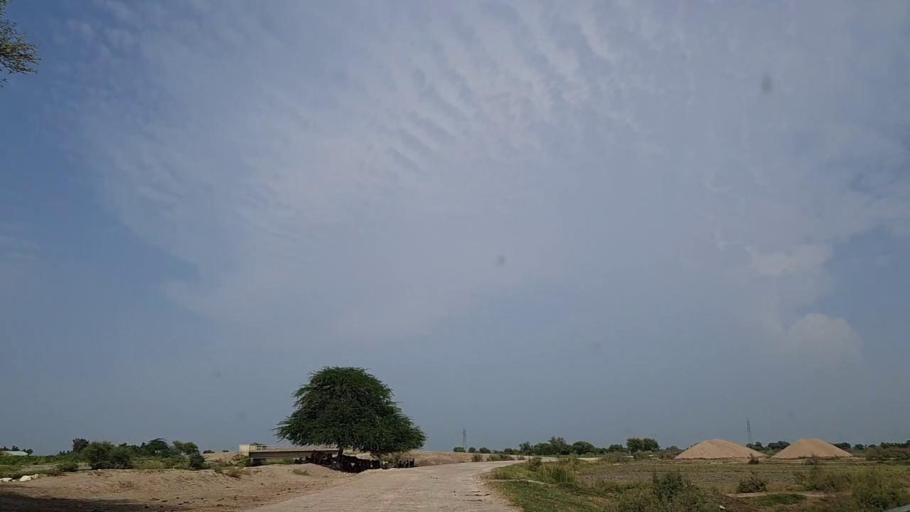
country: PK
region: Sindh
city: Khanpur
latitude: 27.8469
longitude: 69.4200
